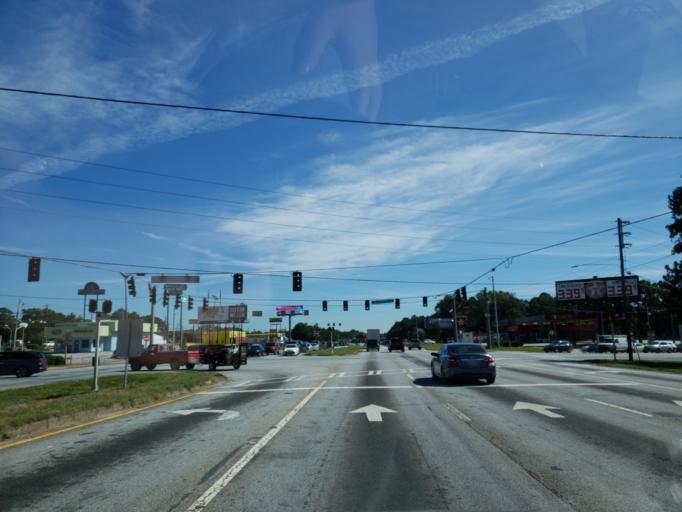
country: US
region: Georgia
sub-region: Clayton County
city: Riverdale
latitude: 33.5859
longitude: -84.3820
